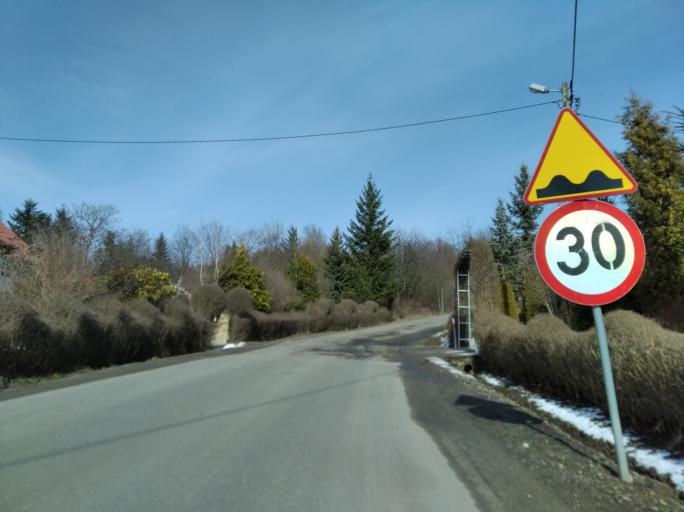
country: PL
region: Subcarpathian Voivodeship
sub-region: Powiat krosnienski
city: Korczyna
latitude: 49.7449
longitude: 21.7904
